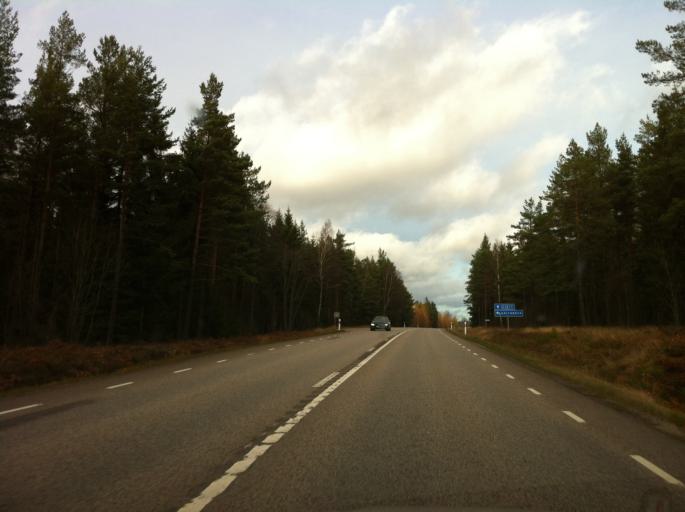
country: SE
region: Kronoberg
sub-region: Vaxjo Kommun
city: Braas
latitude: 57.0698
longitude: 15.1578
